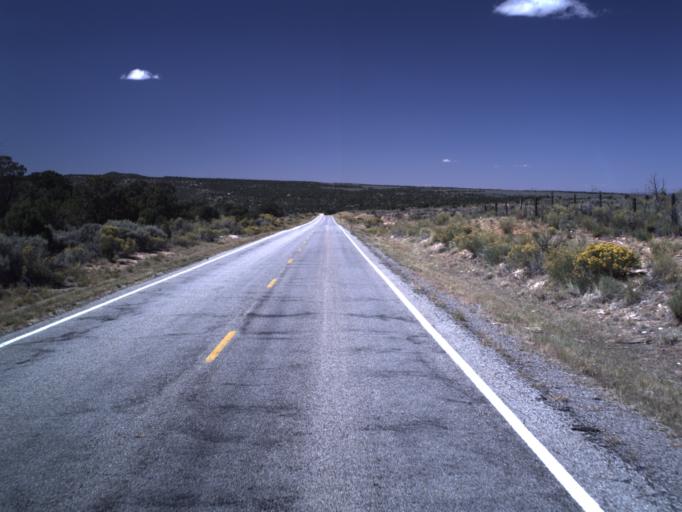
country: US
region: Utah
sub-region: Grand County
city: Moab
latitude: 38.3177
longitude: -109.3195
